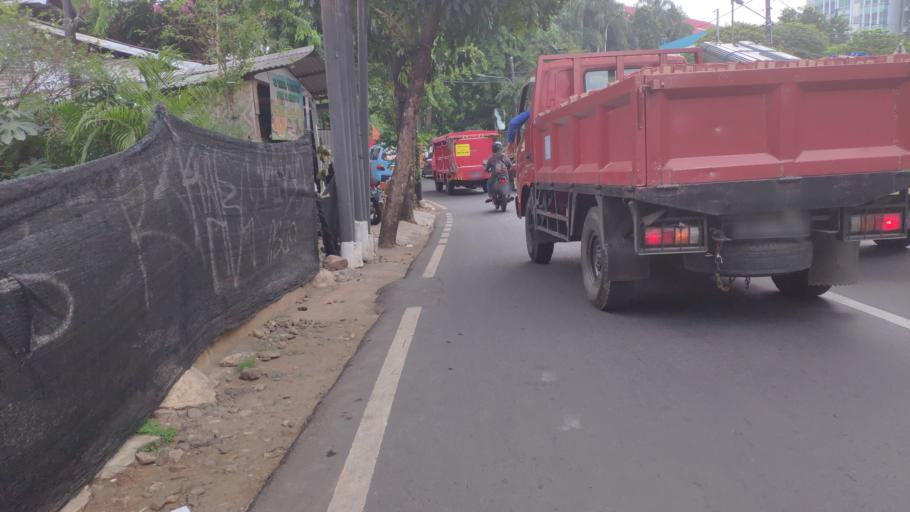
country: ID
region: Jakarta Raya
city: Jakarta
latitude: -6.2784
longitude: 106.8282
